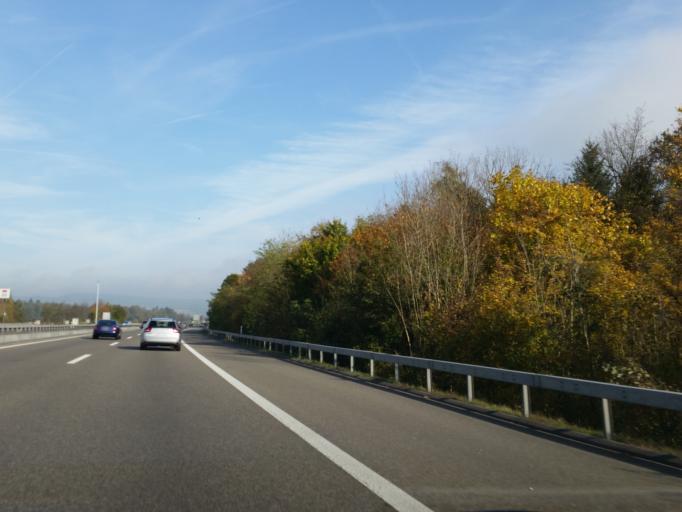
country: CH
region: Aargau
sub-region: Bezirk Lenzburg
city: Othmarsingen
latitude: 47.4190
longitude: 8.2249
